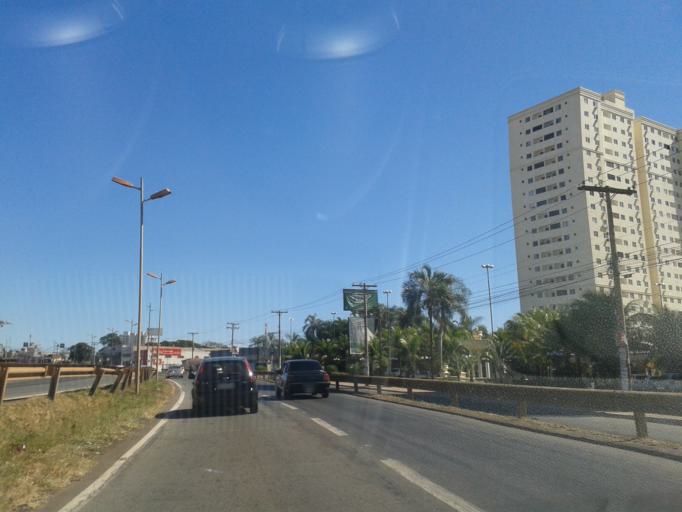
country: BR
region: Goias
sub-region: Goiania
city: Goiania
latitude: -16.6499
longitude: -49.3247
